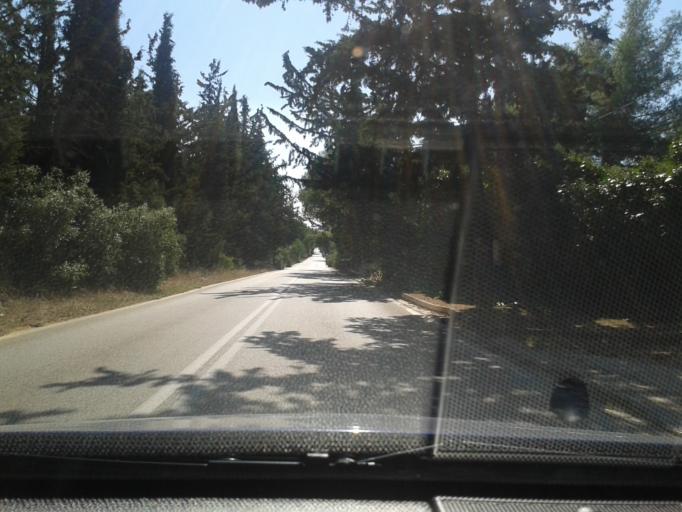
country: GR
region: Attica
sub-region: Nomarchia Anatolikis Attikis
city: Varybobi
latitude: 38.1228
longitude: 23.7968
